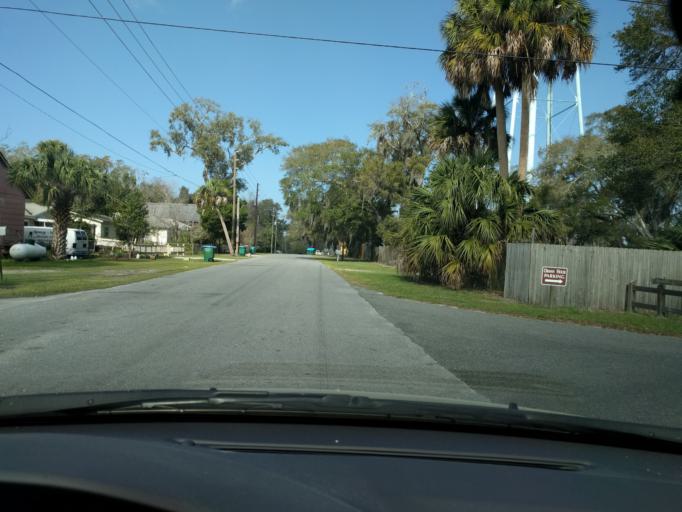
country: US
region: Florida
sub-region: Franklin County
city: Apalachicola
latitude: 29.7300
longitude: -84.9906
